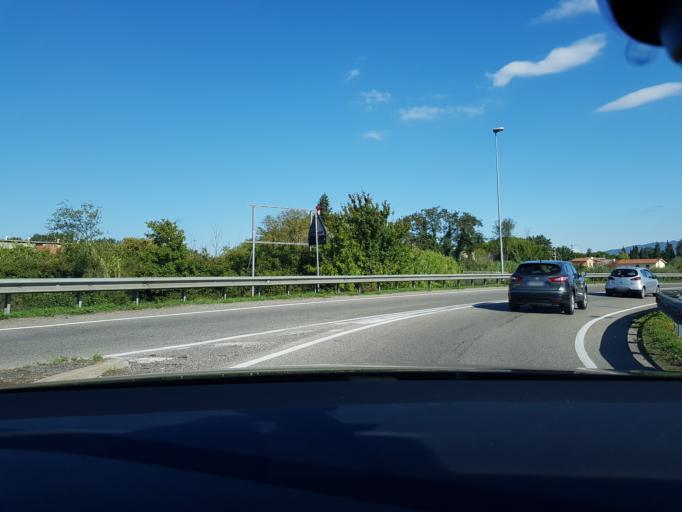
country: IT
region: Tuscany
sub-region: Province of Florence
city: Empoli
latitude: 43.7095
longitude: 10.9169
